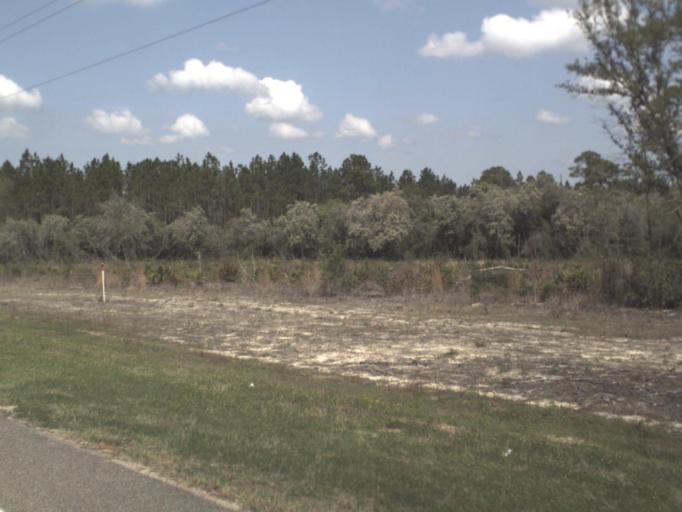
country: US
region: Florida
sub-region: Liberty County
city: Bristol
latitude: 30.4107
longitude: -84.8478
